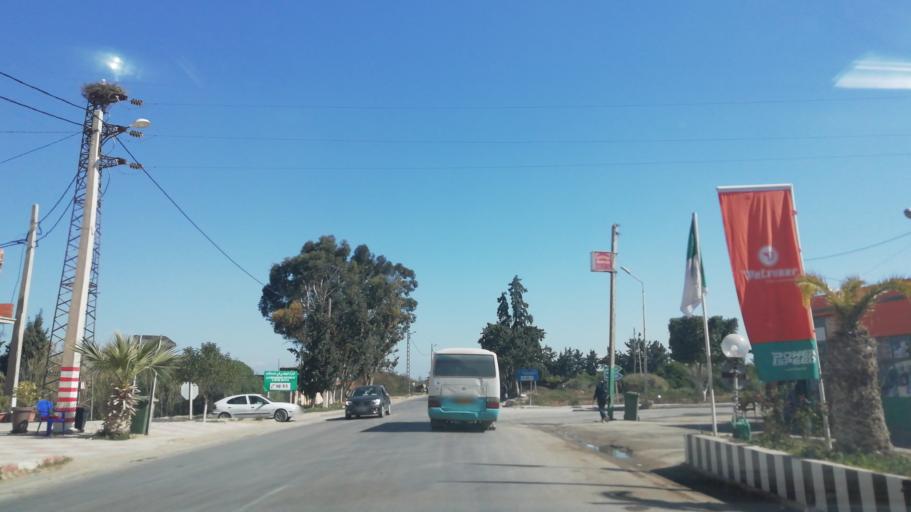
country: DZ
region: Mascara
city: Sig
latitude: 35.5643
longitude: -0.0882
